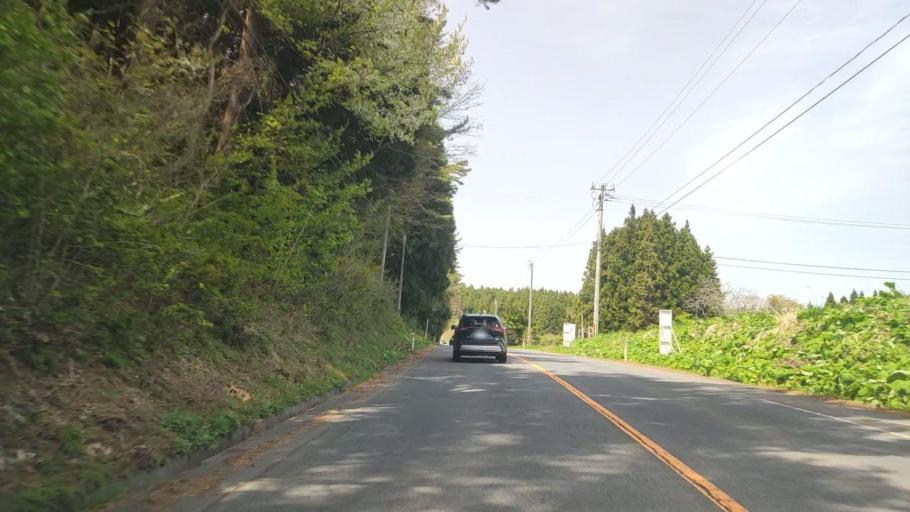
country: JP
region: Aomori
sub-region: Misawa Shi
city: Inuotose
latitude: 40.5667
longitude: 141.3798
